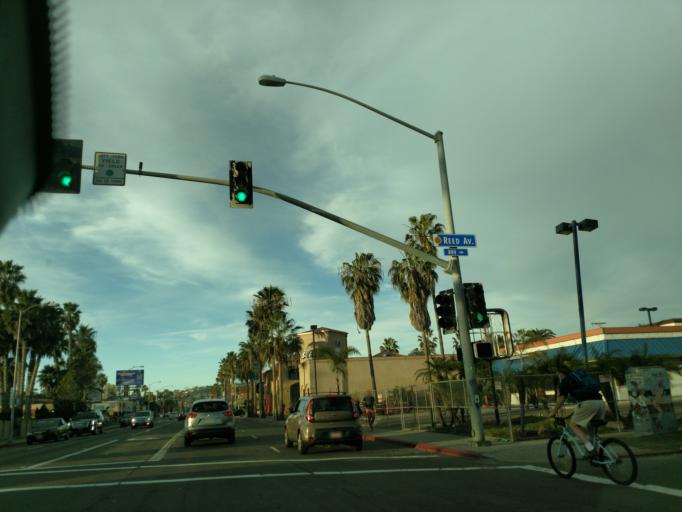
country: US
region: California
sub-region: San Diego County
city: La Jolla
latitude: 32.7927
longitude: -117.2543
